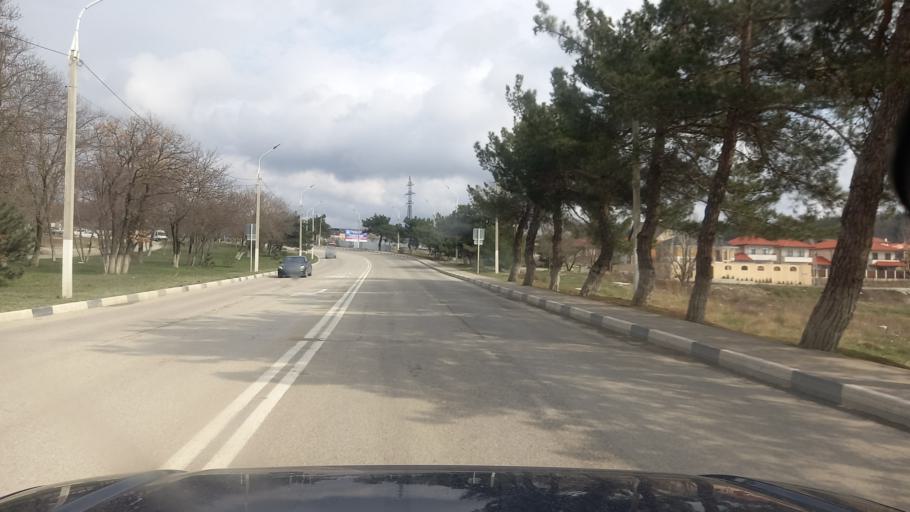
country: RU
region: Krasnodarskiy
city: Gelendzhik
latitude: 44.5539
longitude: 38.1159
